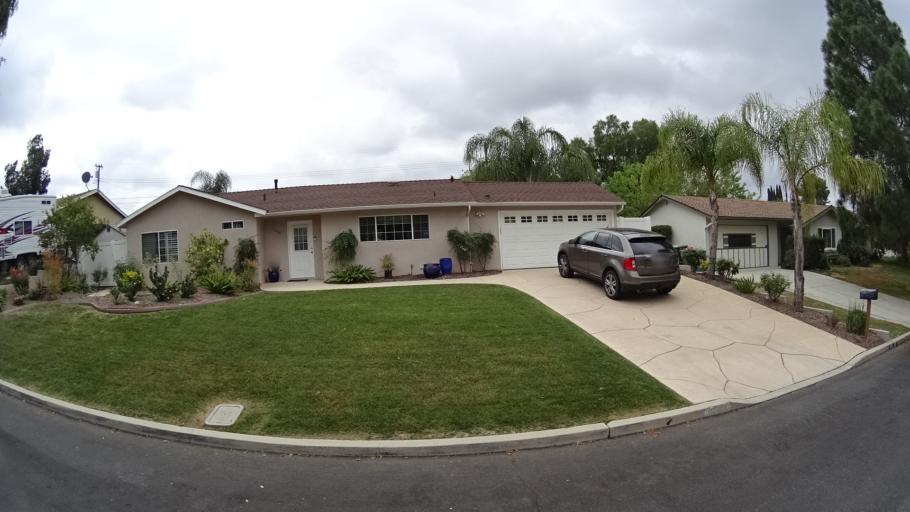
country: US
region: California
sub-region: Ventura County
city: Thousand Oaks
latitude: 34.2111
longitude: -118.8550
